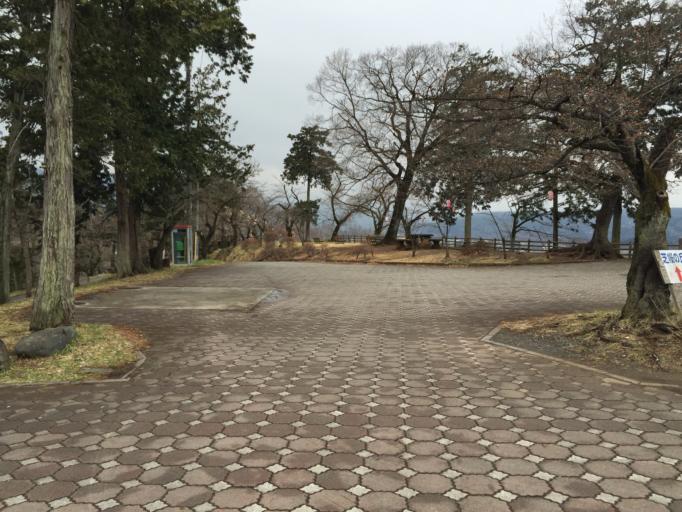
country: JP
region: Saitama
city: Chichibu
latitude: 35.9901
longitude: 139.0904
